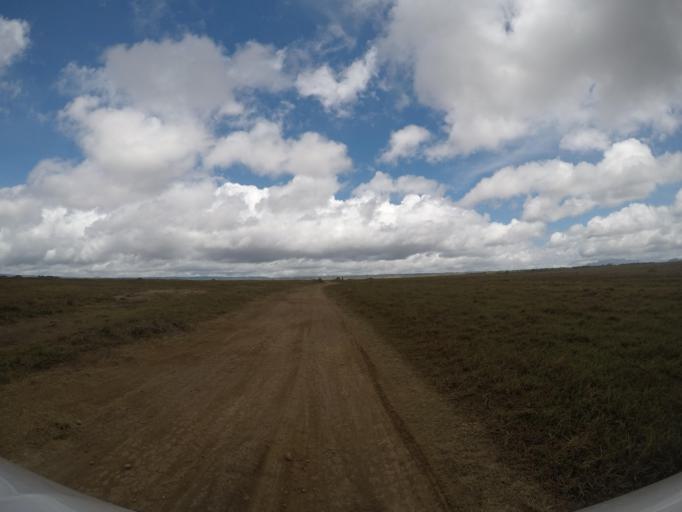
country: TL
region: Lautem
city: Lospalos
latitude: -8.4522
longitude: 126.9860
